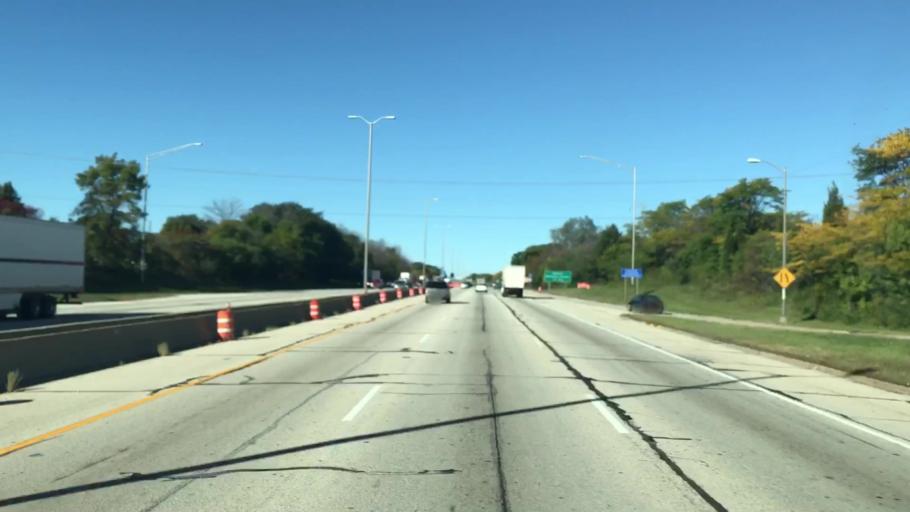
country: US
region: Wisconsin
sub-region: Milwaukee County
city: Greenfield
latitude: 42.9625
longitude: -87.9900
